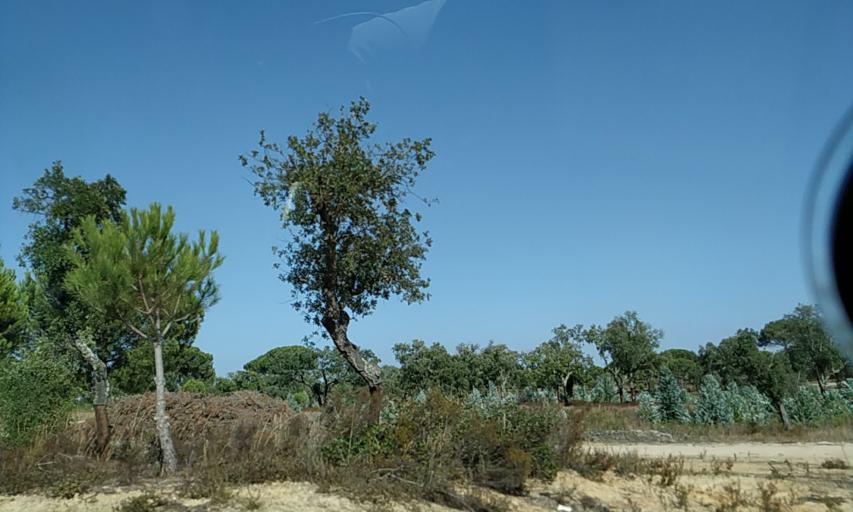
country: PT
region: Santarem
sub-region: Coruche
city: Coruche
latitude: 38.8357
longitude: -8.5588
